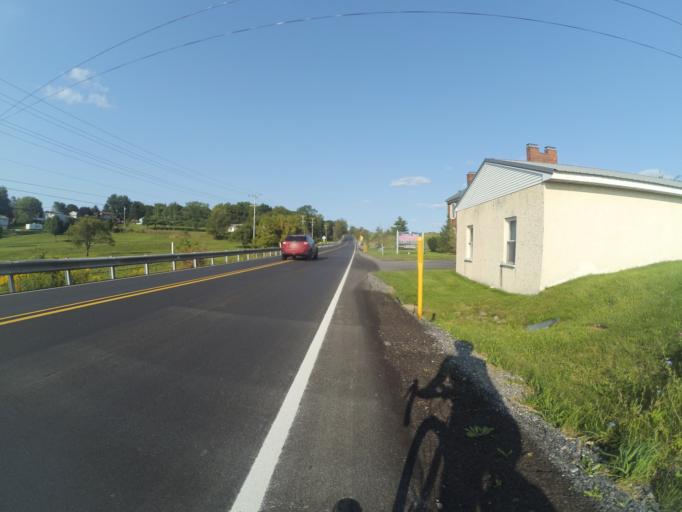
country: US
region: Pennsylvania
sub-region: Centre County
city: Centre Hall
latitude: 40.7984
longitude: -77.7273
